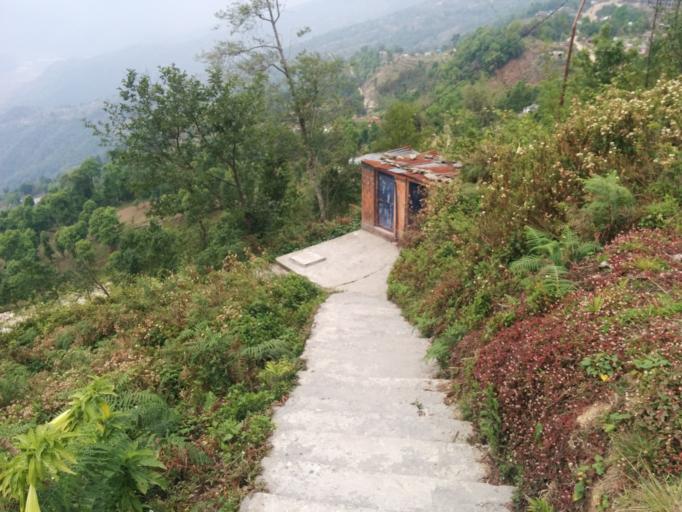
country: NP
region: Western Region
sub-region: Gandaki Zone
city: Pokhara
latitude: 28.2455
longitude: 83.9484
